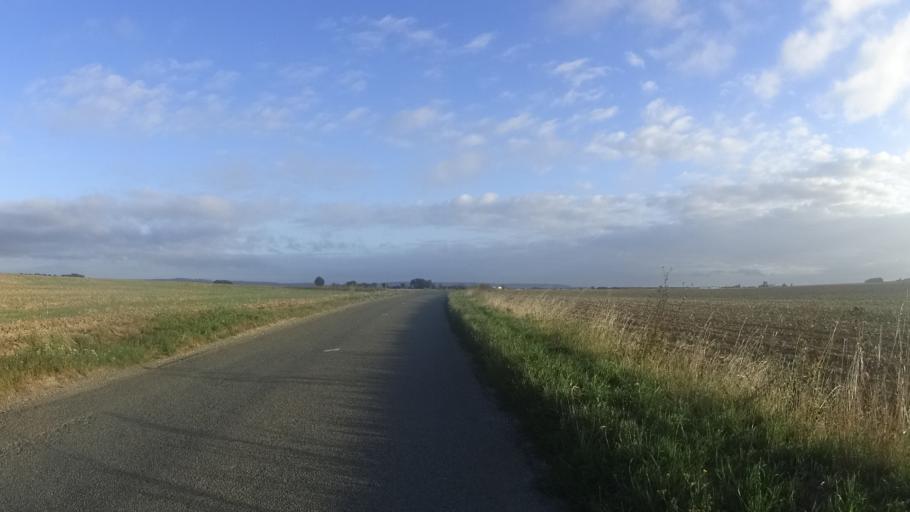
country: FR
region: Picardie
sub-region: Departement de l'Oise
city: Chamant
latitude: 49.1946
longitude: 2.6689
